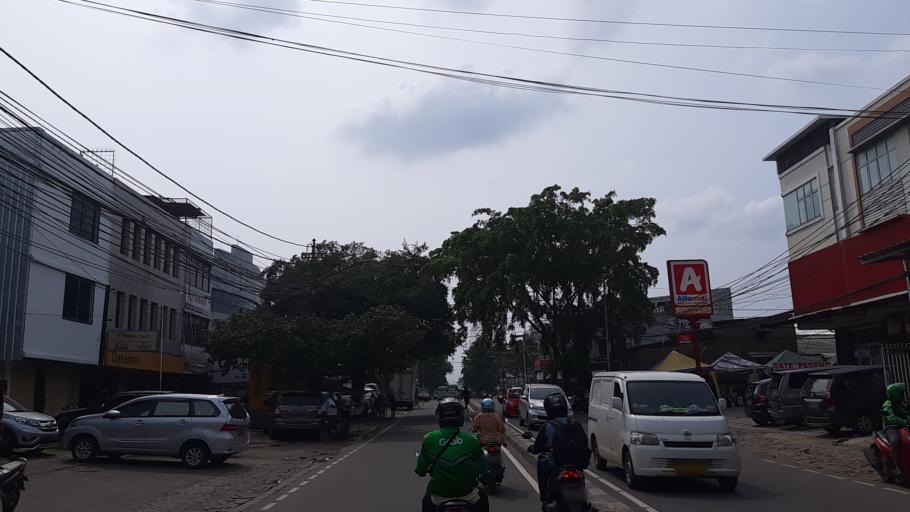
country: ID
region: Jakarta Raya
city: Jakarta
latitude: -6.2069
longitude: 106.7865
